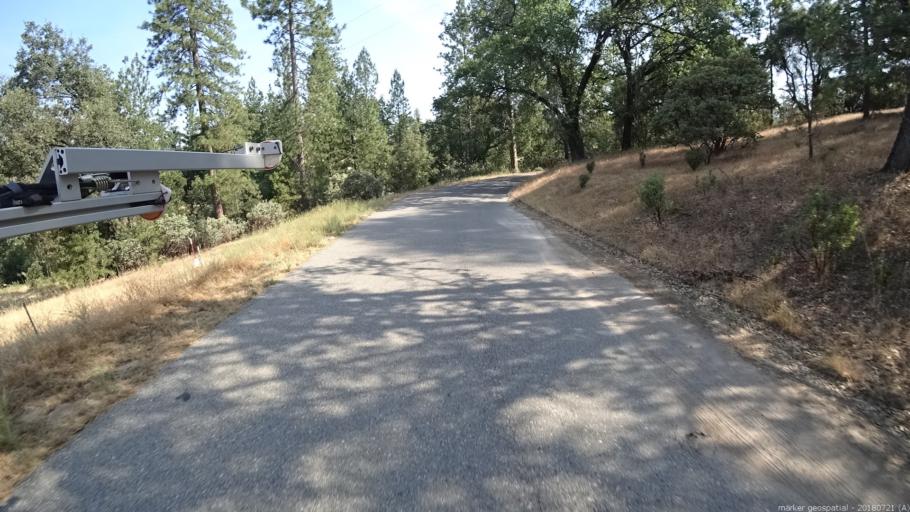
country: US
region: California
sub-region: Madera County
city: Oakhurst
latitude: 37.2370
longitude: -119.5340
